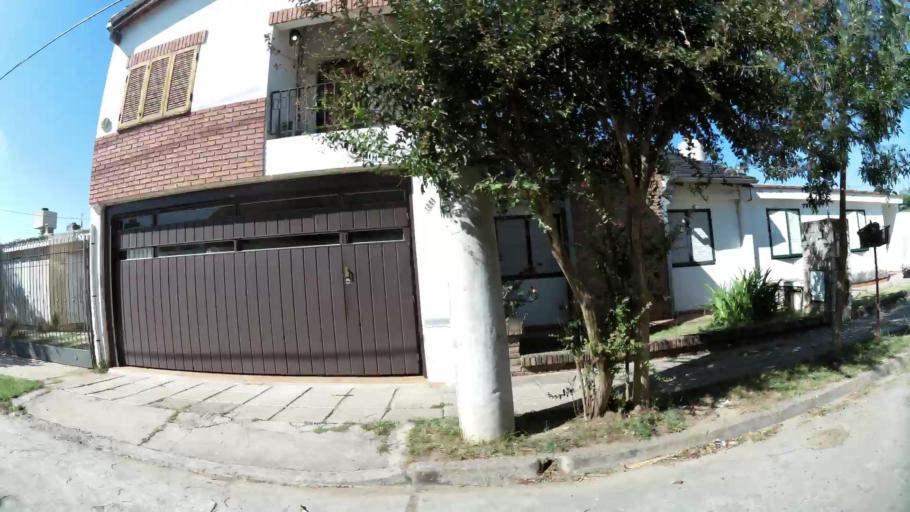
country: AR
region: Cordoba
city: Villa Allende
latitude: -31.3408
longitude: -64.2394
